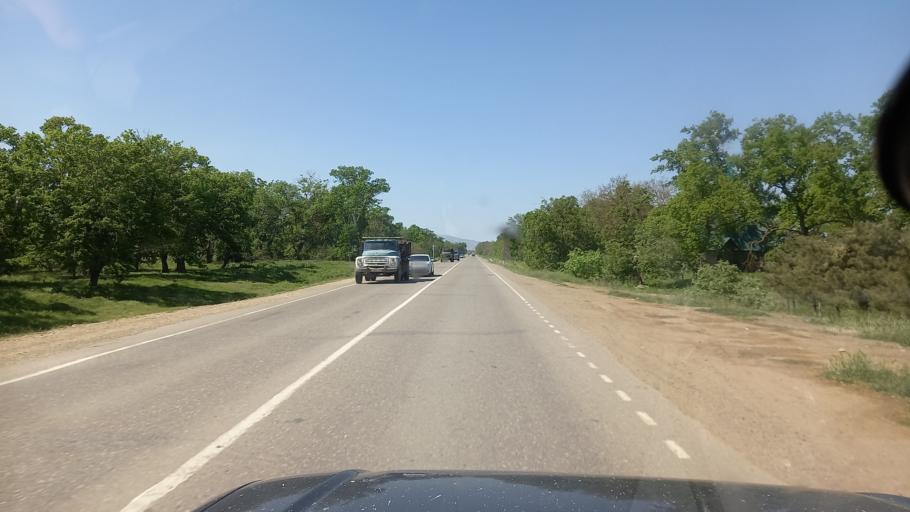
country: RU
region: Dagestan
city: Belidzhi
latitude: 41.8389
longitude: 48.3816
